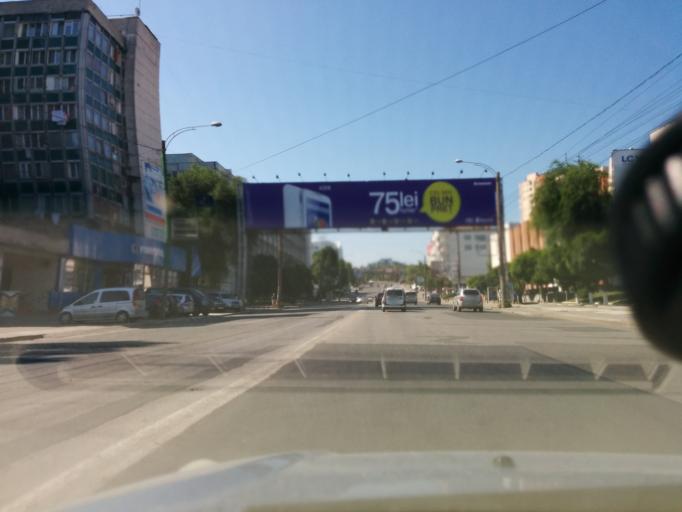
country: MD
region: Chisinau
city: Chisinau
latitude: 47.0090
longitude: 28.8602
